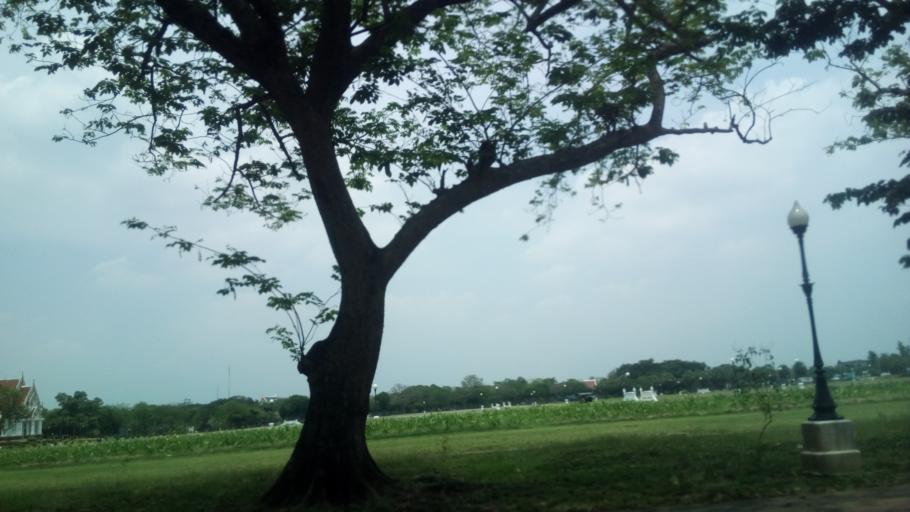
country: TH
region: Bangkok
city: Thawi Watthana
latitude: 13.7754
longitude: 100.3261
